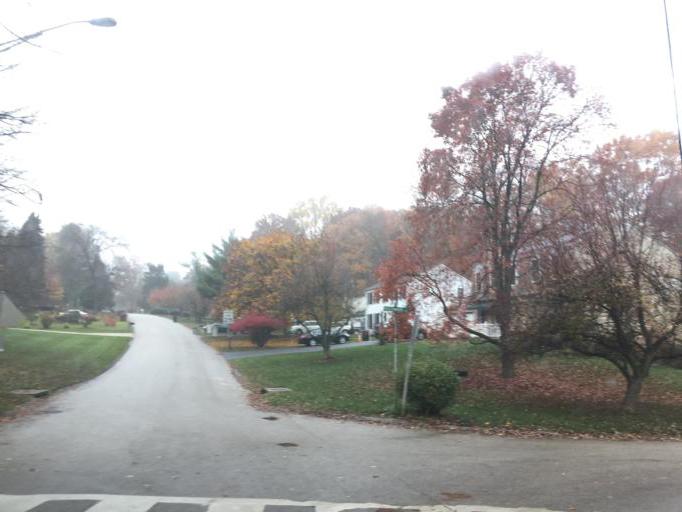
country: US
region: Maryland
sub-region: Howard County
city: Riverside
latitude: 39.1942
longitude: -76.8593
